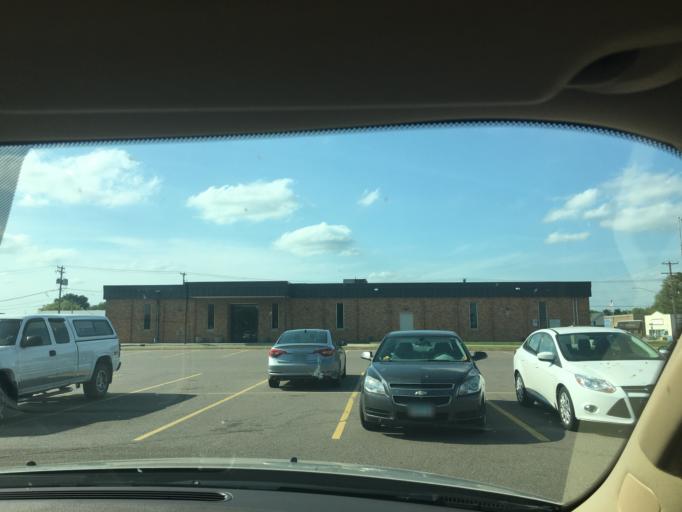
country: US
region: Minnesota
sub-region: Stearns County
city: Saint Cloud
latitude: 45.5658
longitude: -94.1447
